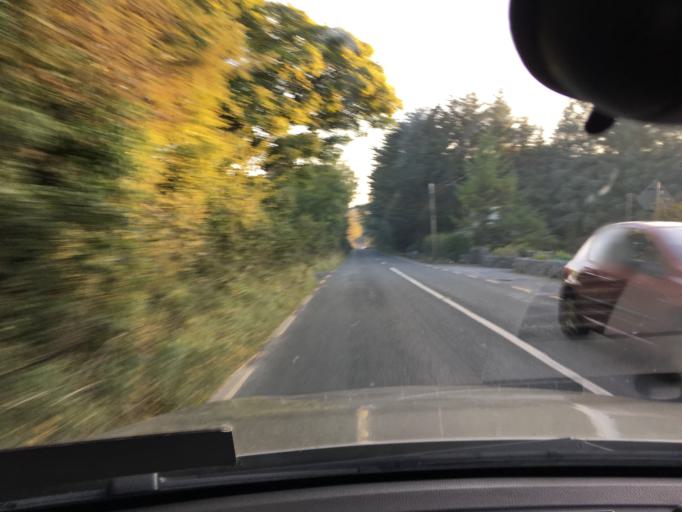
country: IE
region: Connaught
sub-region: County Galway
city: Moycullen
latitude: 53.3840
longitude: -9.2478
